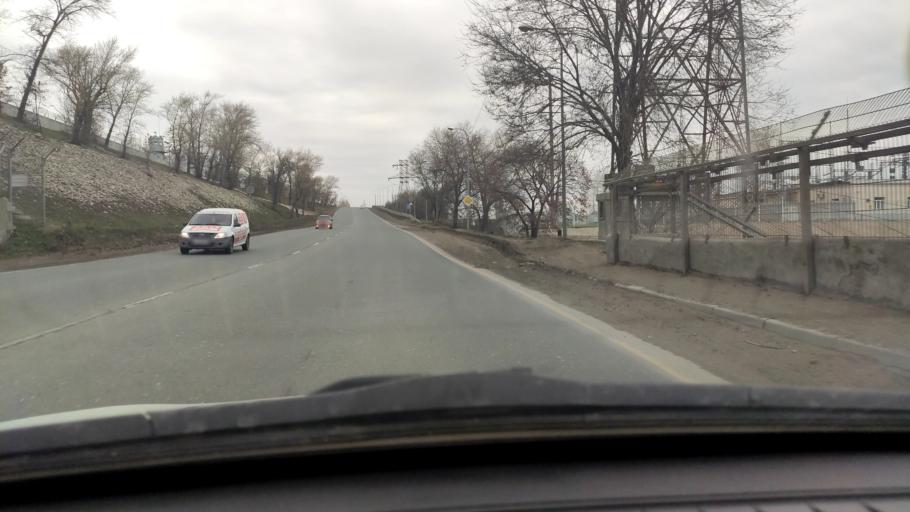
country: RU
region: Samara
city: Zhigulevsk
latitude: 53.4294
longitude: 49.4801
